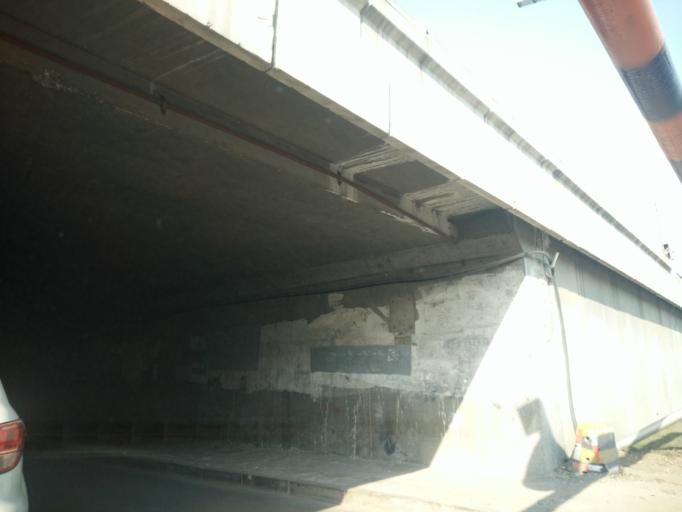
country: CN
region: Beijing
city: Longtan
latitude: 39.8635
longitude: 116.4820
